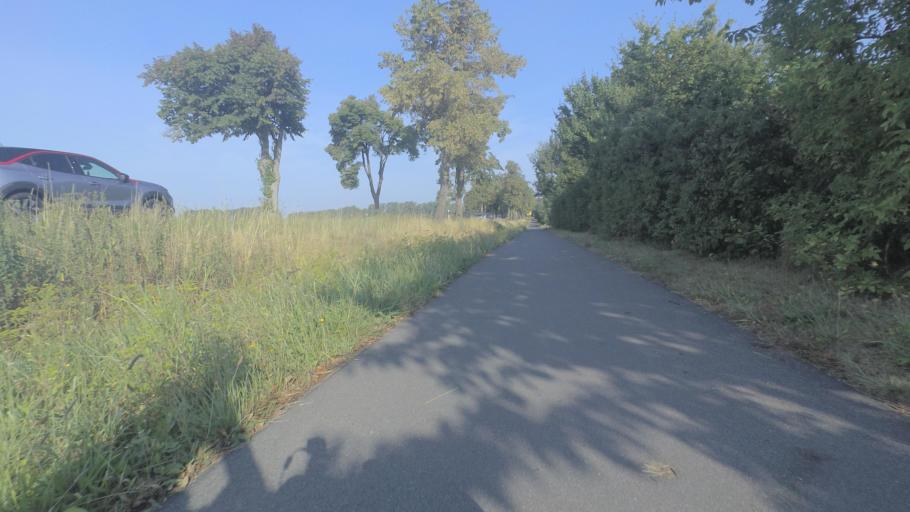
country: DE
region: Mecklenburg-Vorpommern
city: Grimmen
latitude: 54.0979
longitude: 13.0756
